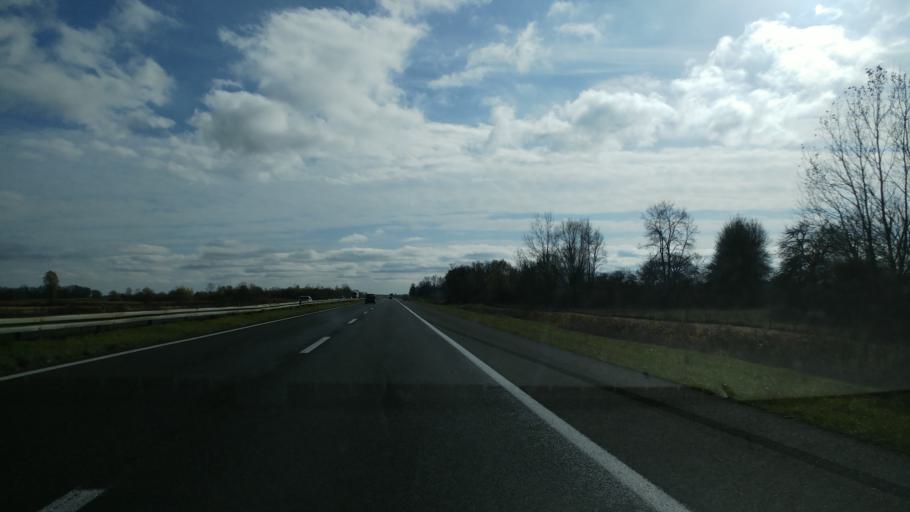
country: HR
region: Zagrebacka
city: Lupoglav
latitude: 45.7161
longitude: 16.3487
